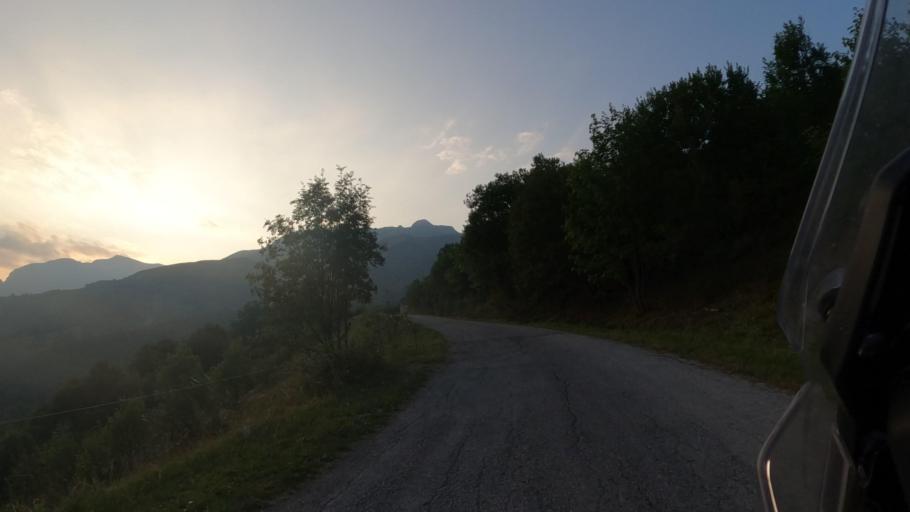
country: IT
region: Piedmont
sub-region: Provincia di Cuneo
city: Limone Piemonte
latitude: 44.1616
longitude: 7.5694
